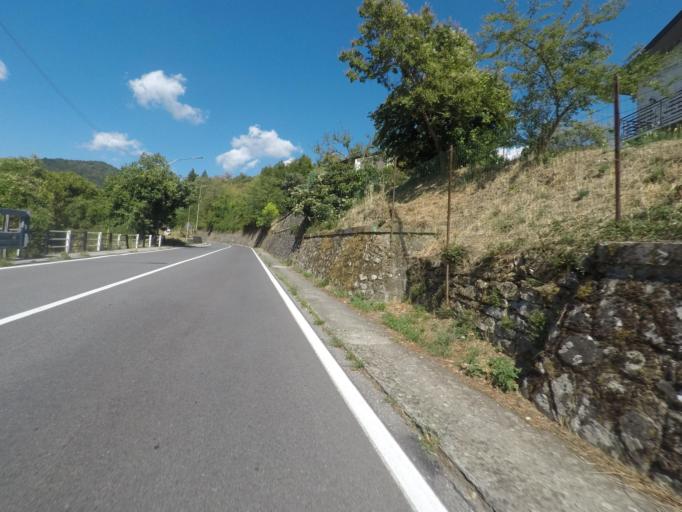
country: IT
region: Tuscany
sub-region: Provincia di Massa-Carrara
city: Fivizzano
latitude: 44.2386
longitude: 10.1284
